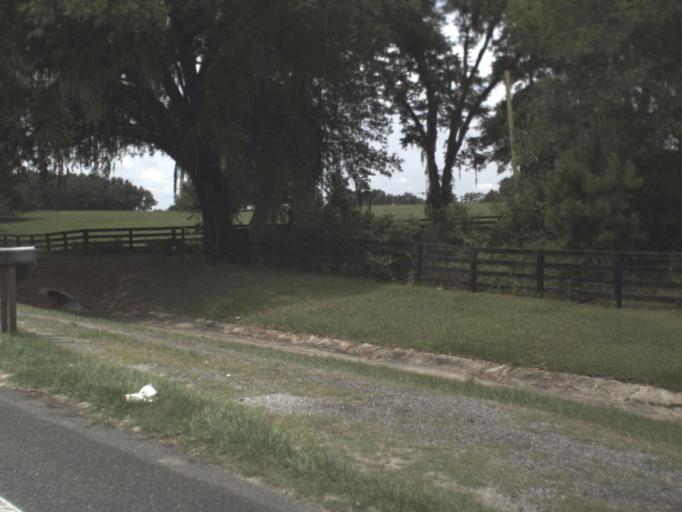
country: US
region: Florida
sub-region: Suwannee County
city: Live Oak
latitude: 30.2213
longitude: -82.9880
